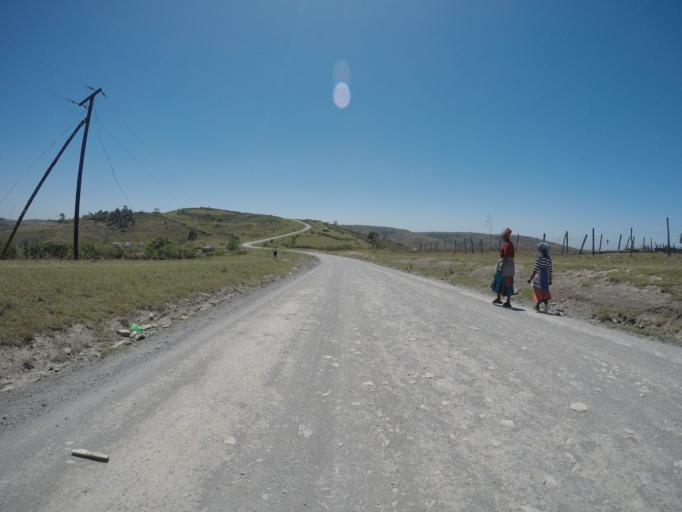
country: ZA
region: Eastern Cape
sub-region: OR Tambo District Municipality
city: Libode
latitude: -31.9806
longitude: 29.0350
